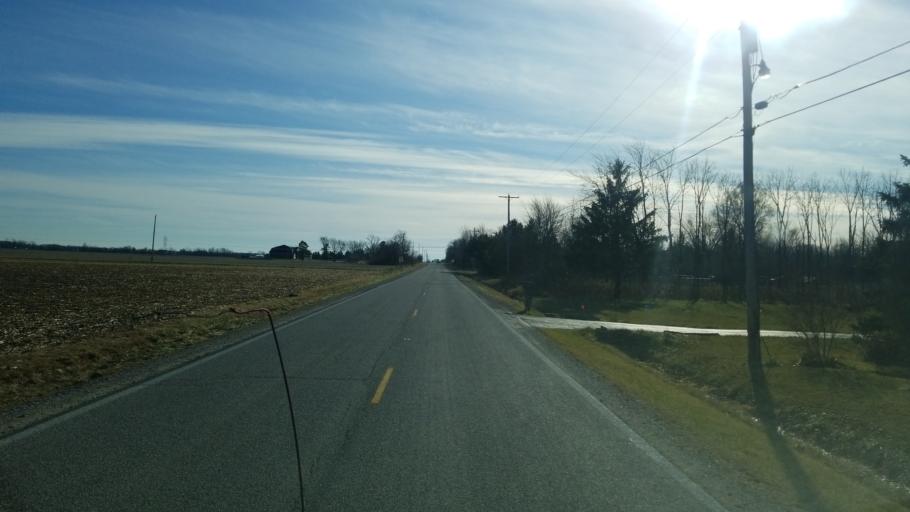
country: US
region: Ohio
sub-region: Sandusky County
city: Stony Prairie
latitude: 41.3646
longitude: -83.2230
